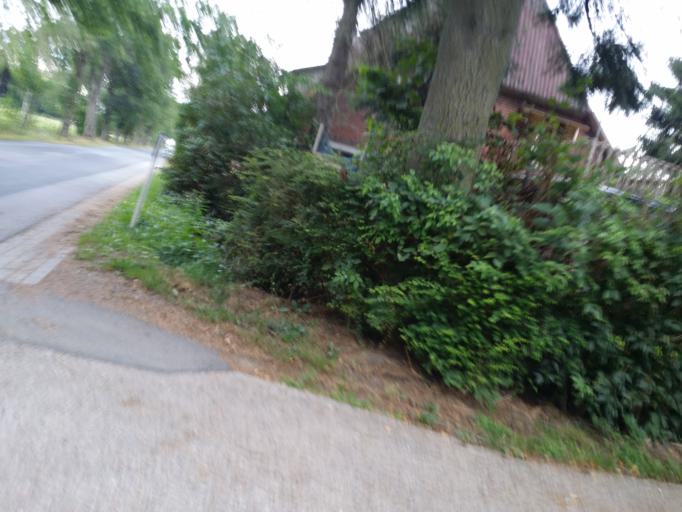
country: DE
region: Lower Saxony
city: Osten
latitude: 53.7426
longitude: 9.2270
